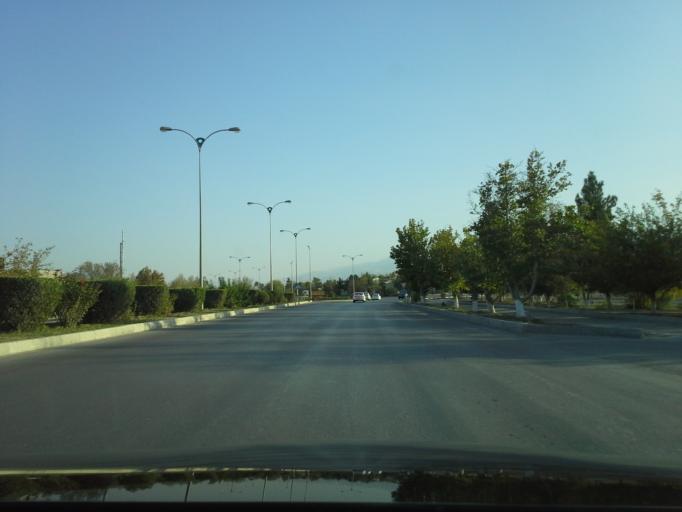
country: TM
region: Ahal
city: Abadan
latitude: 38.0367
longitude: 58.1879
